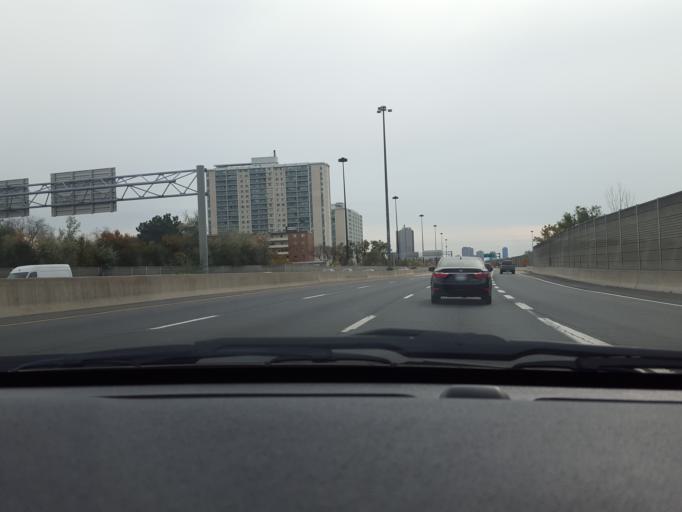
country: CA
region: Ontario
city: Willowdale
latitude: 43.7634
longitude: -79.3372
